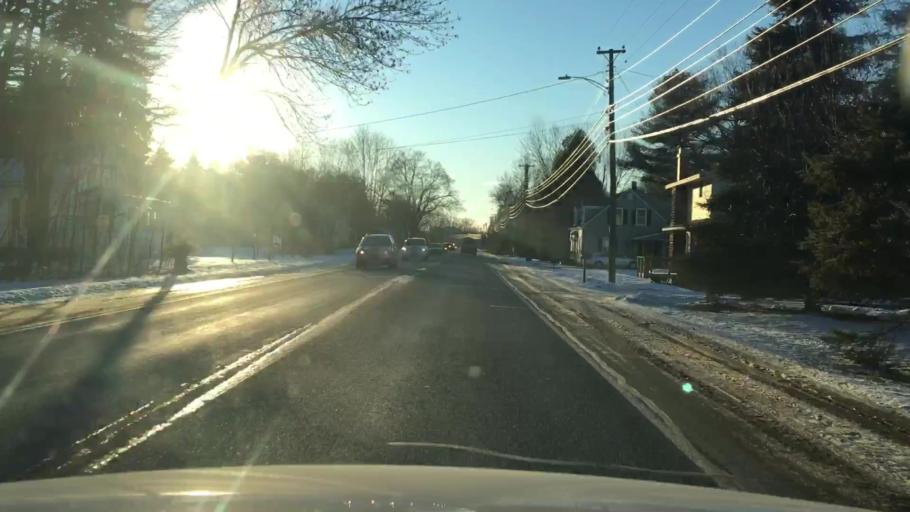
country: US
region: Maine
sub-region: Penobscot County
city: Veazie
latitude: 44.8176
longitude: -68.7229
